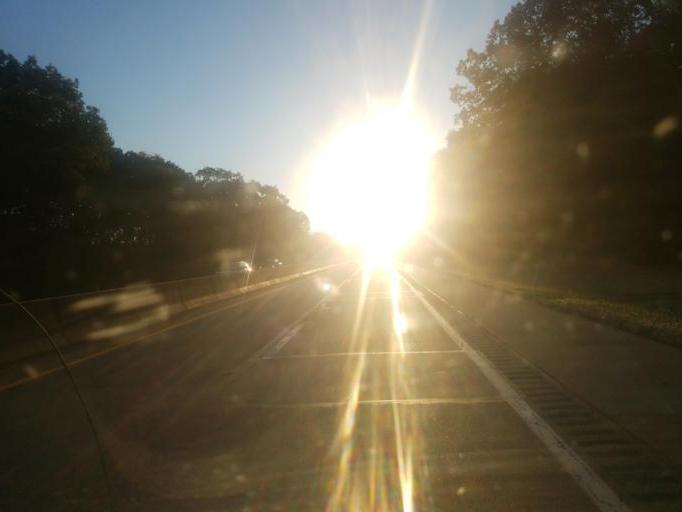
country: US
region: Pennsylvania
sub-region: Beaver County
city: Beaver Falls
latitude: 40.7870
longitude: -80.2526
